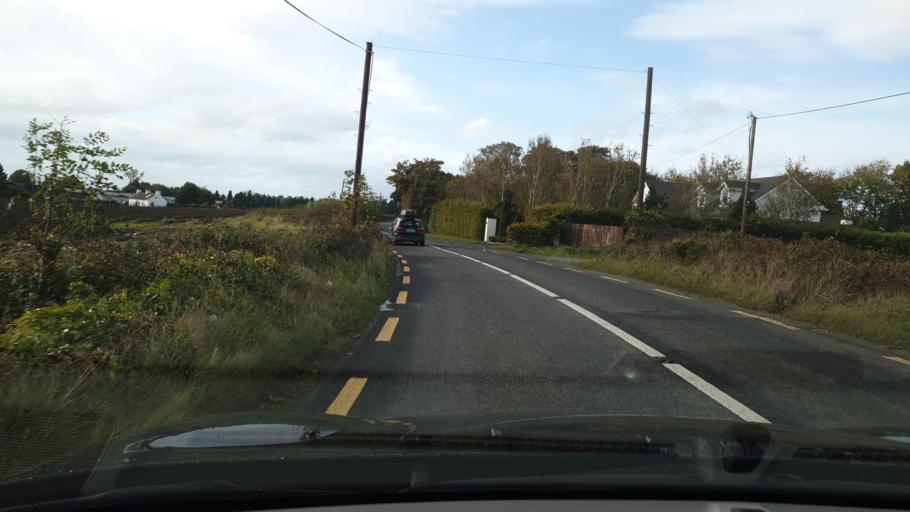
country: IE
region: Leinster
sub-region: An Mhi
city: Ratoath
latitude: 53.5169
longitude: -6.4942
